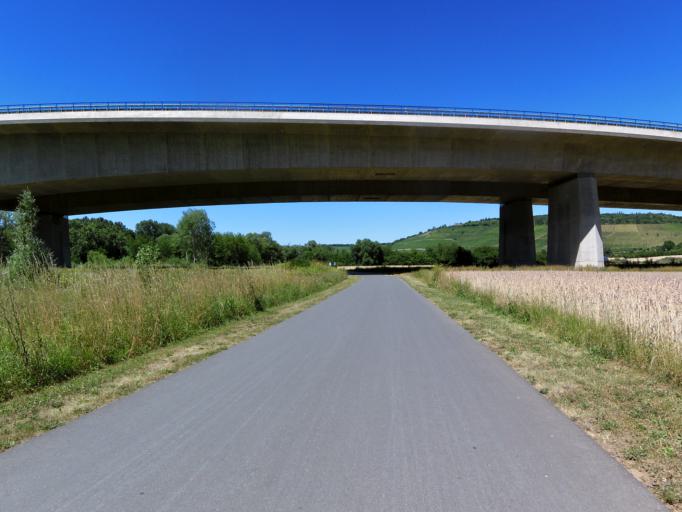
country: DE
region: Bavaria
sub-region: Regierungsbezirk Unterfranken
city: Eibelstadt
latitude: 49.7380
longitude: 9.9876
